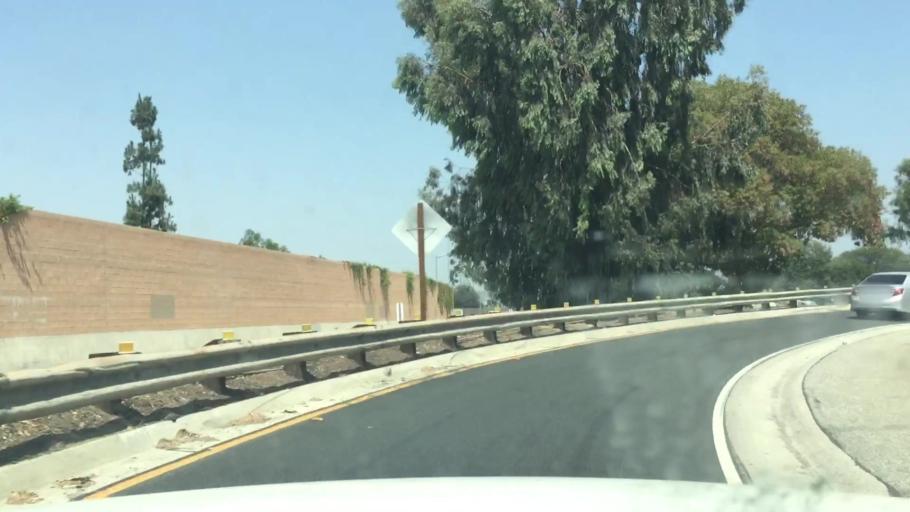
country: US
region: California
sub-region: Los Angeles County
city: West Whittier-Los Nietos
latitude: 33.9751
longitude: -118.0810
